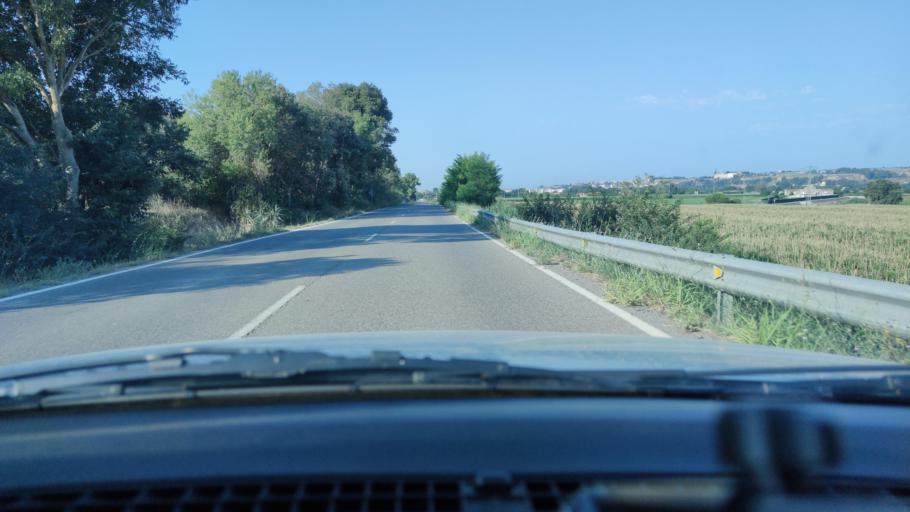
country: ES
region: Catalonia
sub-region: Provincia de Lleida
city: Balaguer
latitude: 41.8086
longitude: 0.8291
